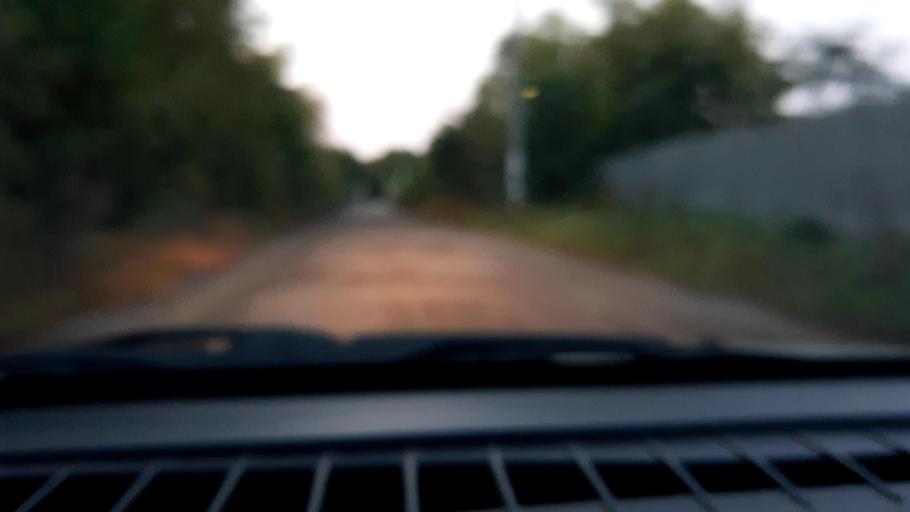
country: RU
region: Nizjnij Novgorod
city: Gorbatovka
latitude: 56.2582
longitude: 43.8289
